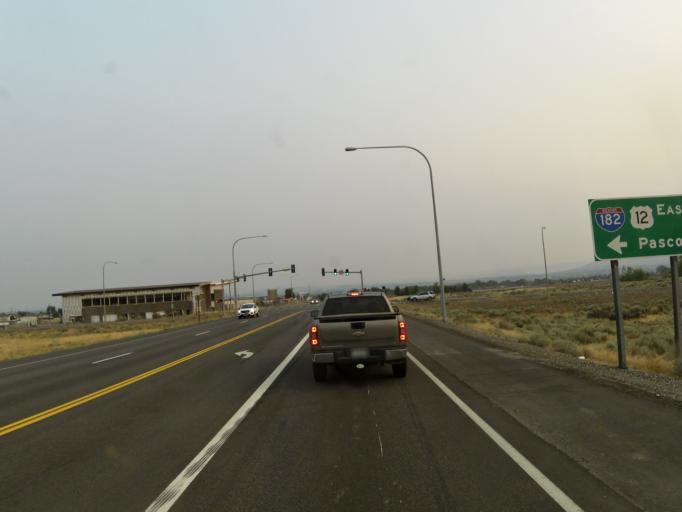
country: US
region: Washington
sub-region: Franklin County
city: West Pasco
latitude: 46.2743
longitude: -119.2217
